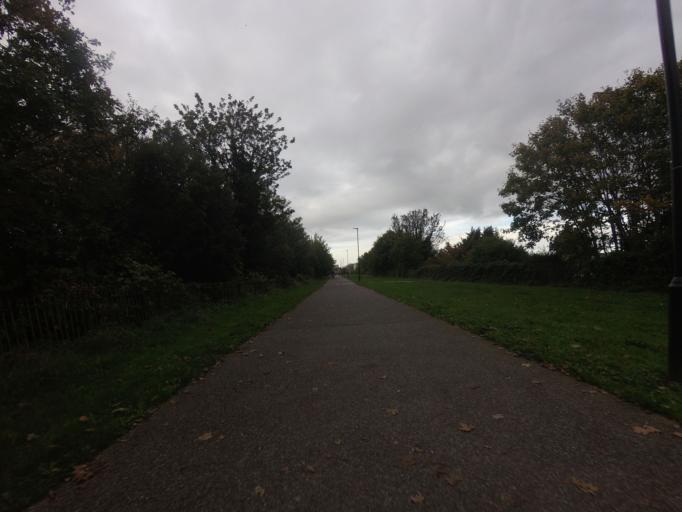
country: GB
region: England
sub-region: Greater London
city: East Ham
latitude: 51.5286
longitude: 0.0155
